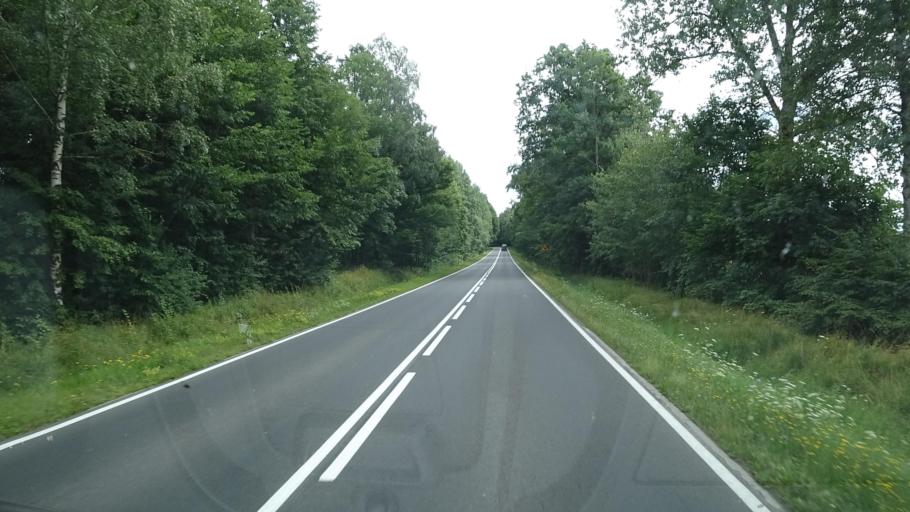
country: PL
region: Warmian-Masurian Voivodeship
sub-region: Powiat elcki
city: Stare Juchy
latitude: 53.7956
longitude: 22.2198
